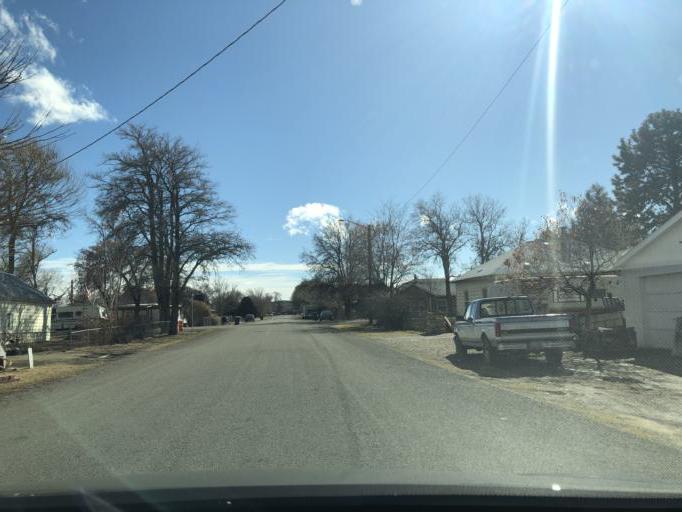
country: US
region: Utah
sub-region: Carbon County
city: East Carbon City
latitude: 38.9945
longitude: -110.1610
